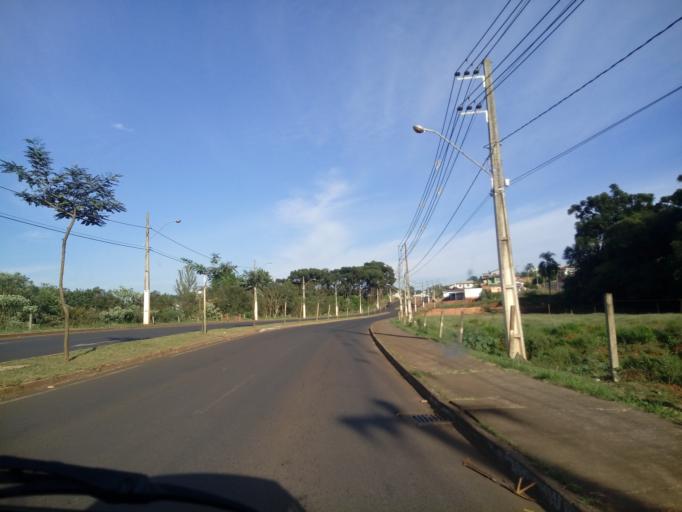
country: BR
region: Santa Catarina
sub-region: Chapeco
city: Chapeco
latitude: -27.0896
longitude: -52.6684
